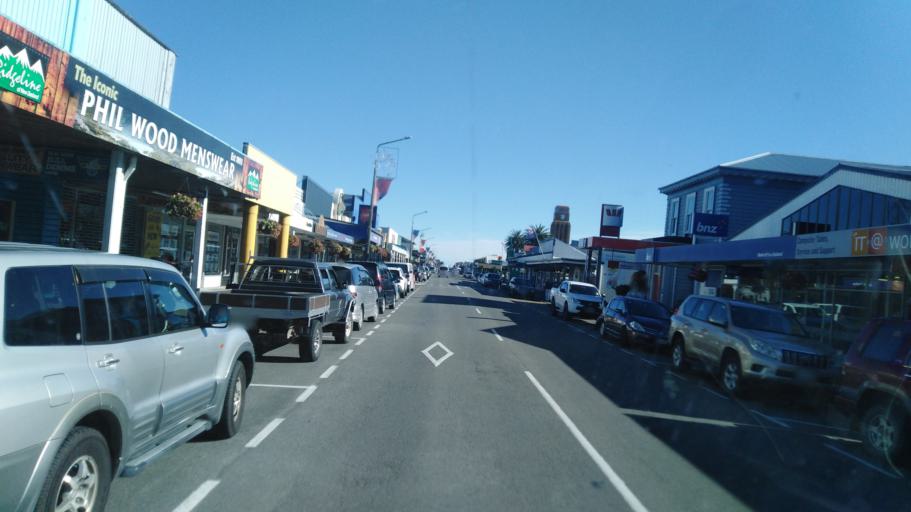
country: NZ
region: West Coast
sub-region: Buller District
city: Westport
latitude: -41.7552
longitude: 171.5986
